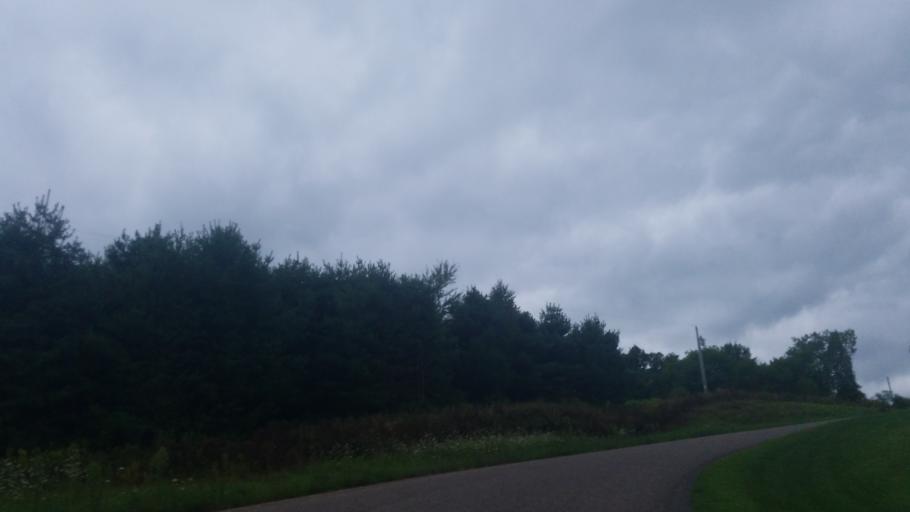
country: US
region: Wisconsin
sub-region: Dunn County
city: Menomonie
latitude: 44.8125
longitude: -91.9577
